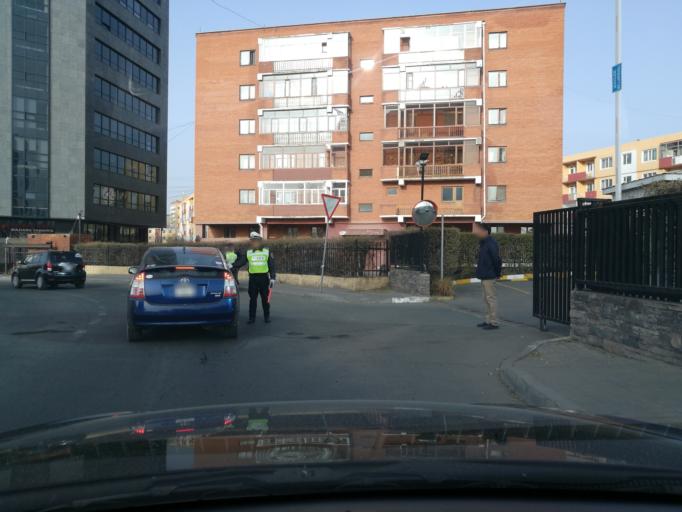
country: MN
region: Ulaanbaatar
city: Ulaanbaatar
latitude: 47.9108
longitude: 106.9137
